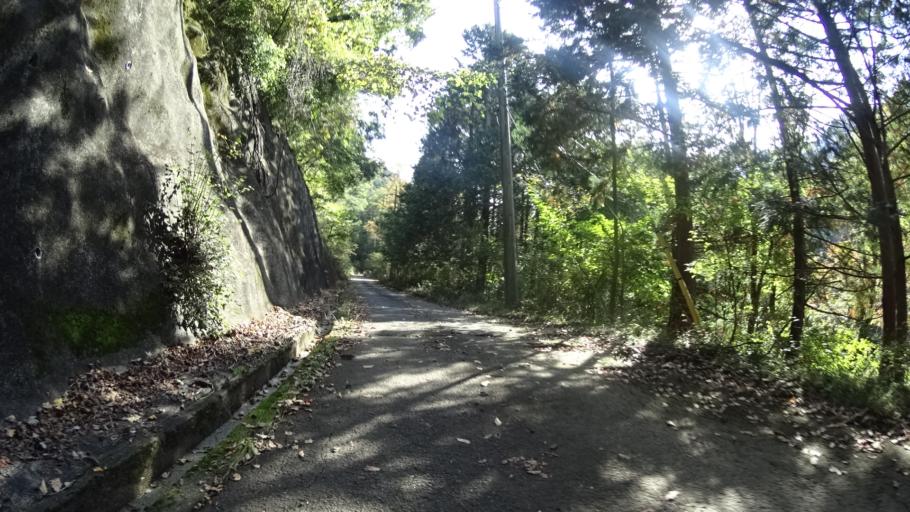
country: JP
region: Yamanashi
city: Otsuki
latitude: 35.5818
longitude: 138.9752
